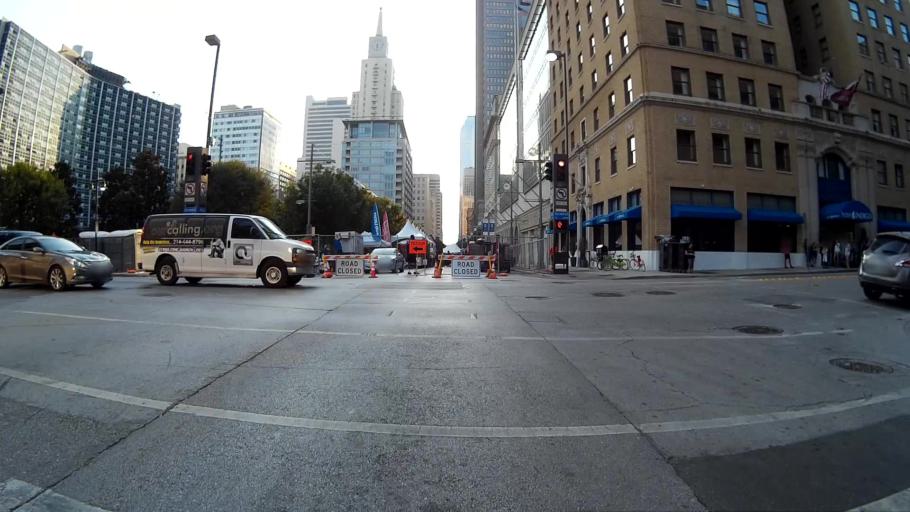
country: US
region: Texas
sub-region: Dallas County
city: Dallas
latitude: 32.7818
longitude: -96.7940
